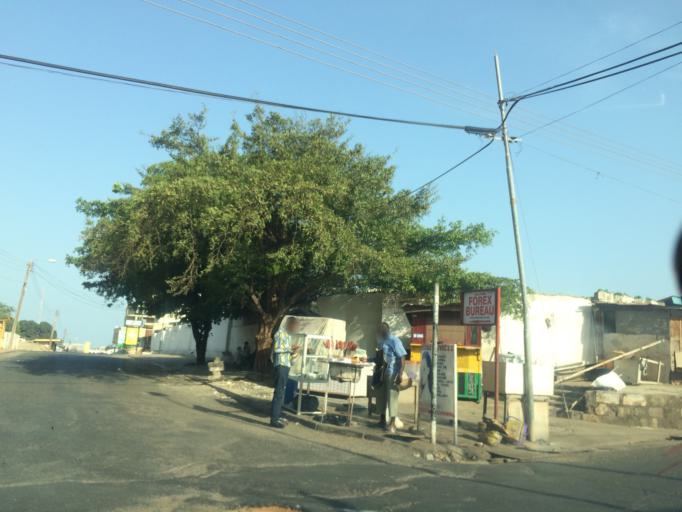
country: GH
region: Greater Accra
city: Accra
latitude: 5.5614
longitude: -0.1859
